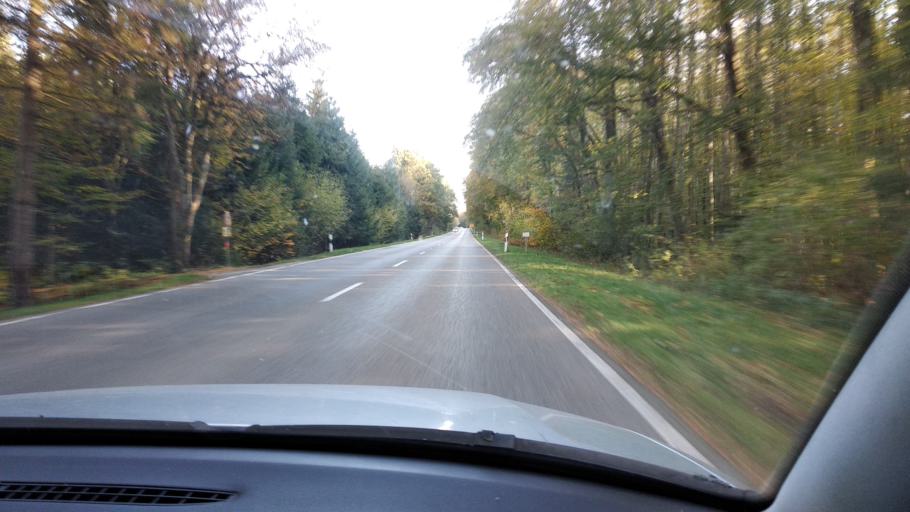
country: DE
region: Bavaria
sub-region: Upper Bavaria
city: Grasbrunn
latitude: 48.0546
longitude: 11.7577
